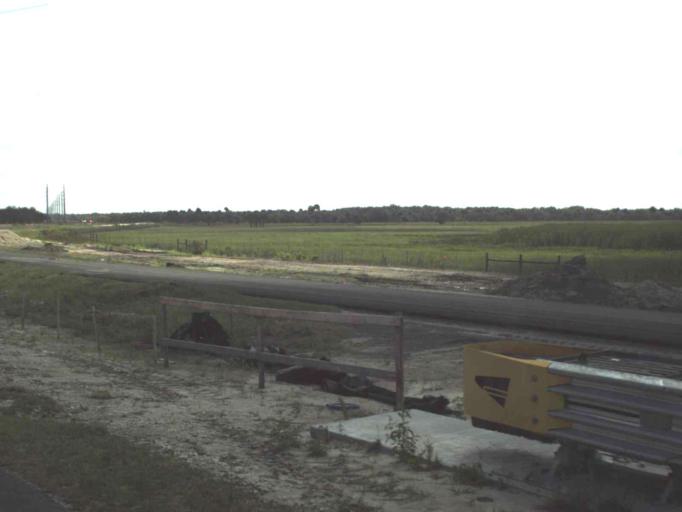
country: US
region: Florida
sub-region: Seminole County
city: Midway
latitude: 28.8063
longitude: -81.2082
